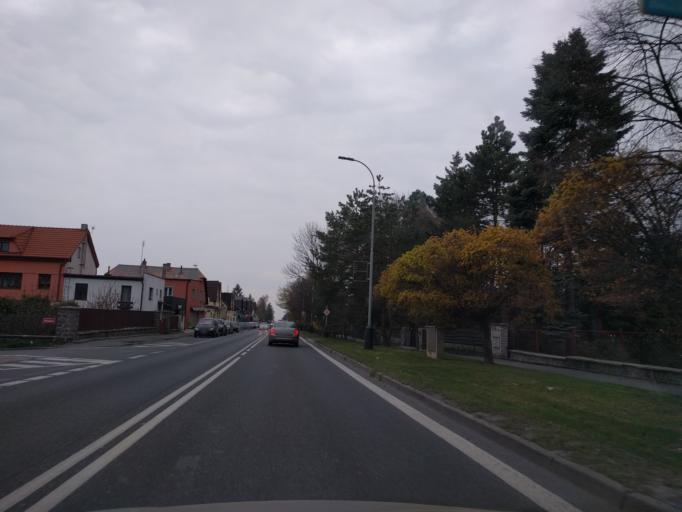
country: CZ
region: Central Bohemia
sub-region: Okres Praha-Vychod
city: Ricany
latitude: 49.9935
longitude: 14.6868
